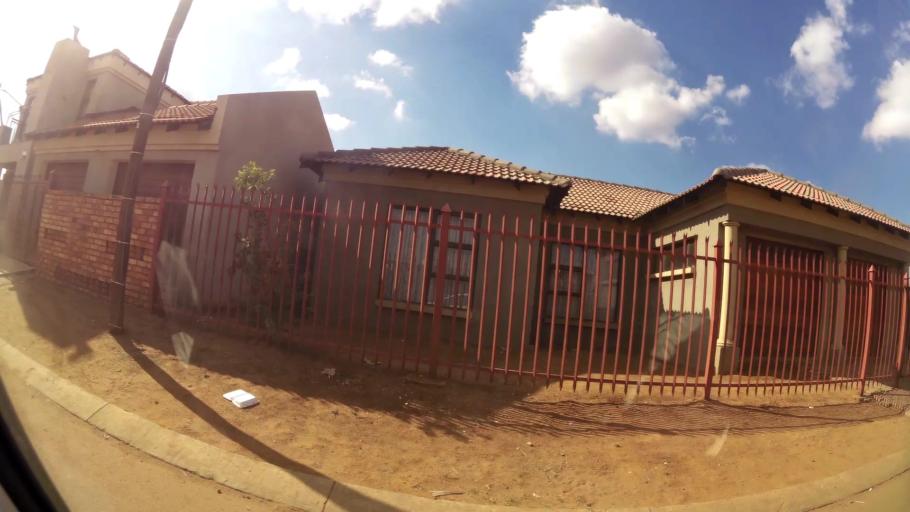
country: ZA
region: Gauteng
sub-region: City of Tshwane Metropolitan Municipality
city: Cullinan
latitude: -25.7007
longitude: 28.4143
